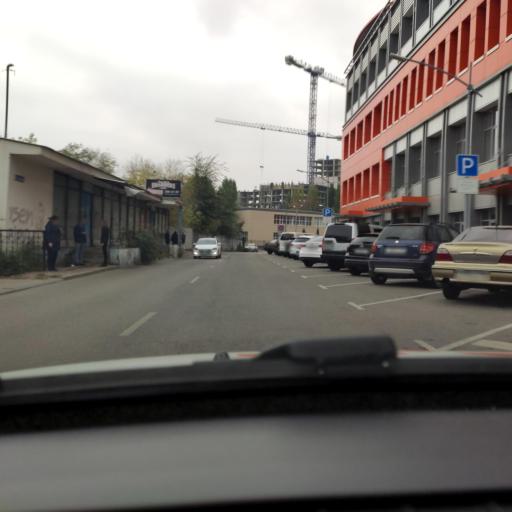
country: RU
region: Voronezj
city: Voronezh
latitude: 51.6559
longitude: 39.1938
